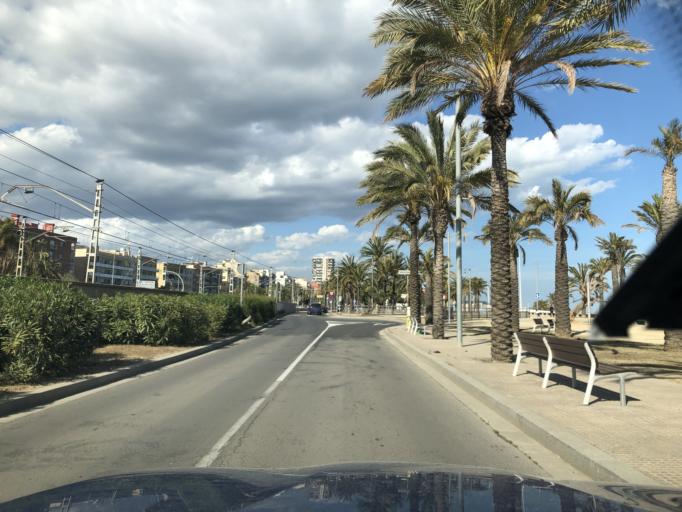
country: ES
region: Catalonia
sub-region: Provincia de Barcelona
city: Mataro
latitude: 41.5352
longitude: 2.4484
